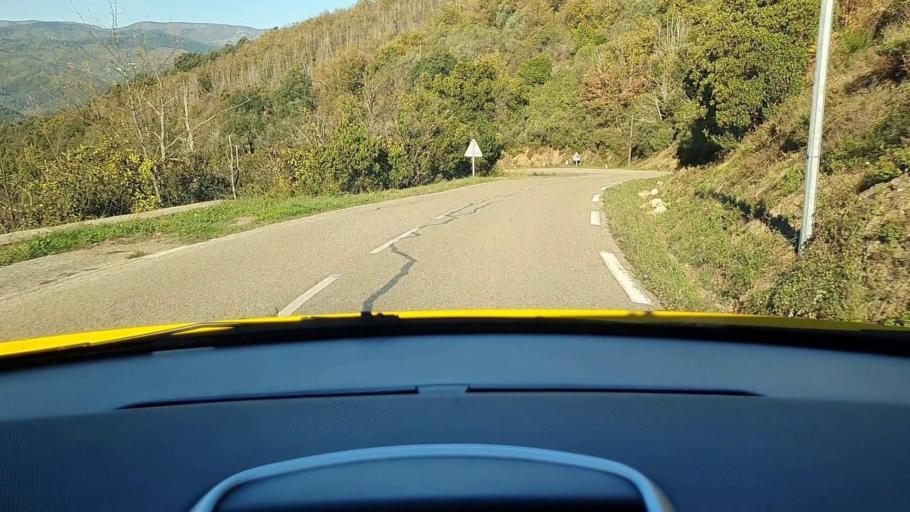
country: FR
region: Languedoc-Roussillon
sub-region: Departement du Gard
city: Sumene
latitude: 43.9882
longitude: 3.7003
